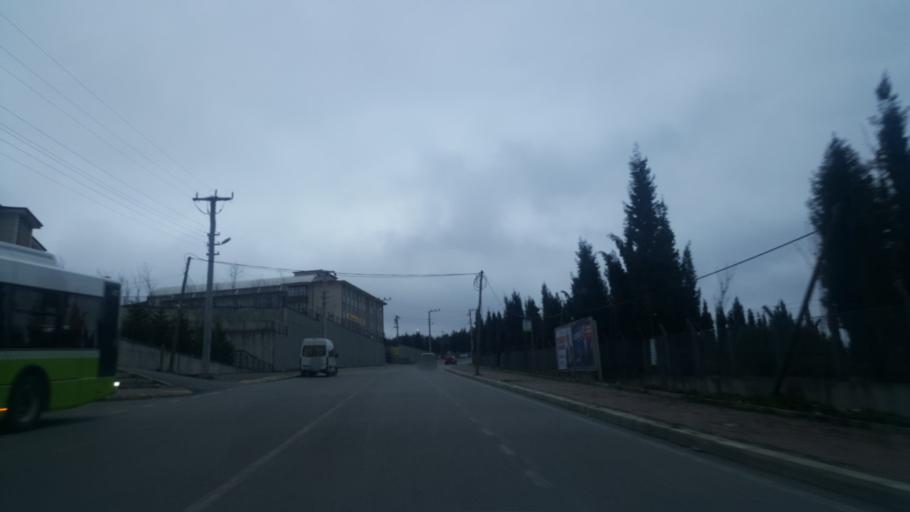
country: TR
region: Kocaeli
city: Tavsancil
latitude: 40.7955
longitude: 29.5520
